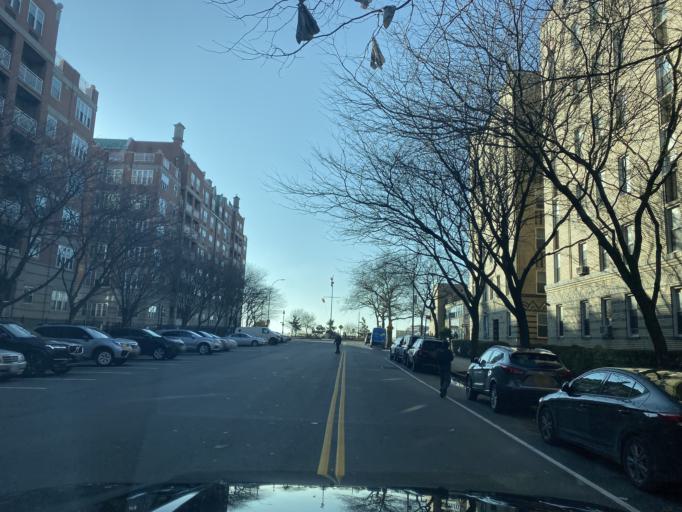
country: US
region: New York
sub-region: Kings County
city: Coney Island
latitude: 40.5765
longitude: -73.9596
